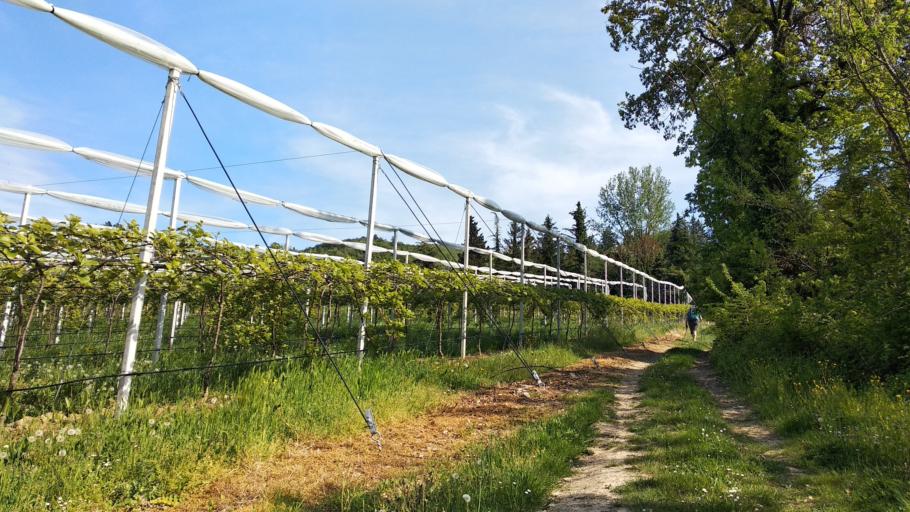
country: IT
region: Emilia-Romagna
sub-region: Provincia di Ravenna
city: Fognano
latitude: 44.2318
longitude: 11.7182
